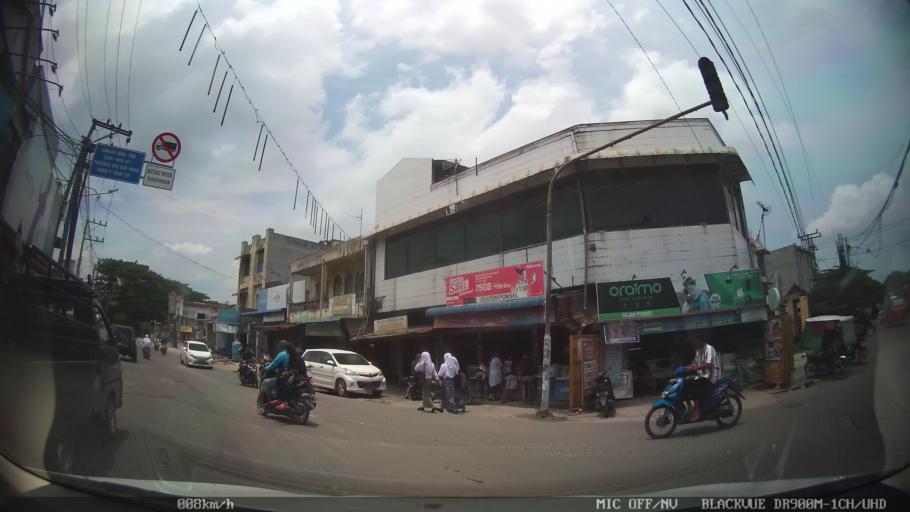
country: ID
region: North Sumatra
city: Labuhan Deli
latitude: 3.6877
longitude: 98.6673
